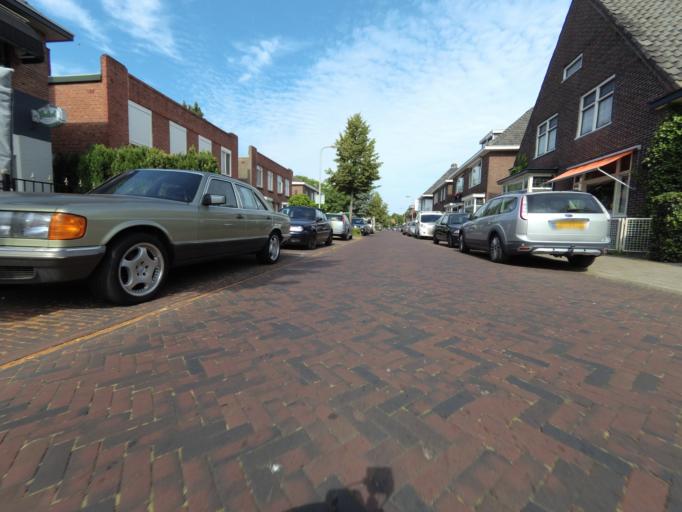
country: NL
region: Overijssel
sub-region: Gemeente Enschede
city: Enschede
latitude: 52.2175
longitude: 6.8658
